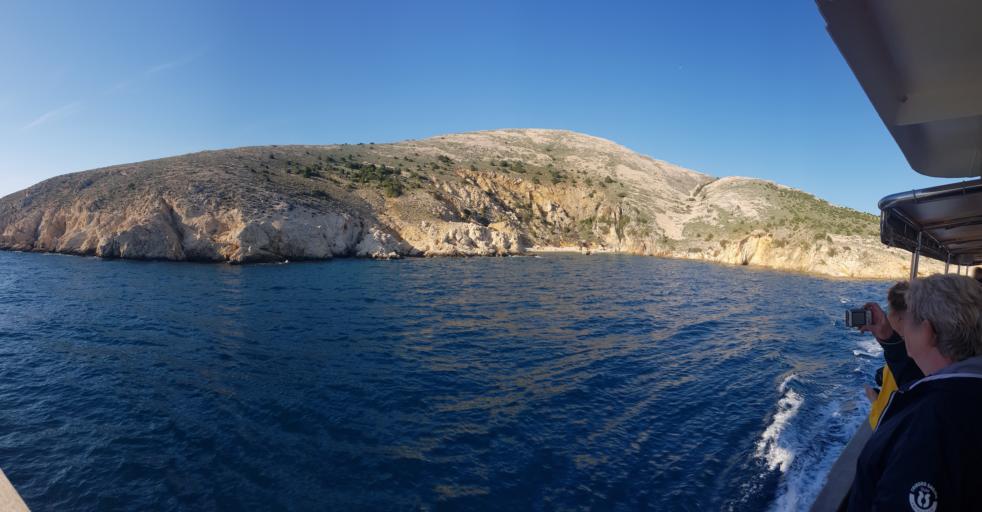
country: HR
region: Primorsko-Goranska
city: Punat
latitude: 44.9658
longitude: 14.6461
